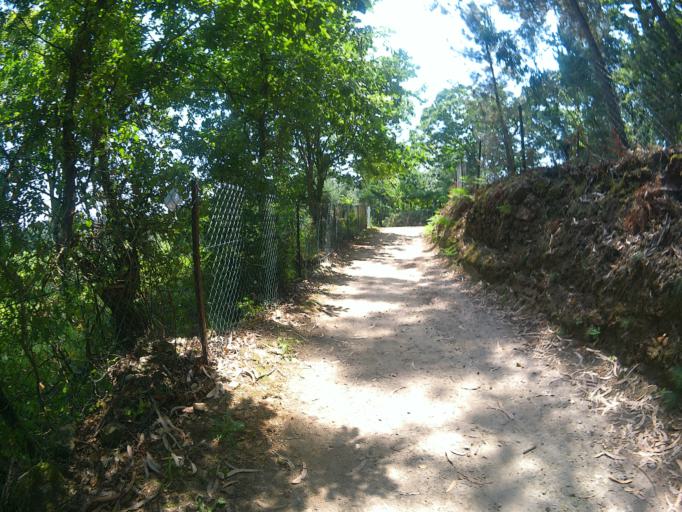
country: PT
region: Viana do Castelo
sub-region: Ponte de Lima
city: Ponte de Lima
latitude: 41.7745
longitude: -8.5680
